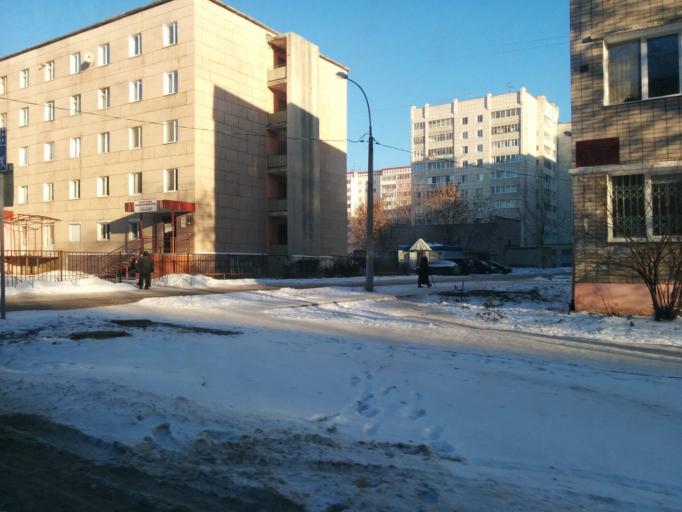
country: RU
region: Perm
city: Kultayevo
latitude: 58.0173
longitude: 55.9791
